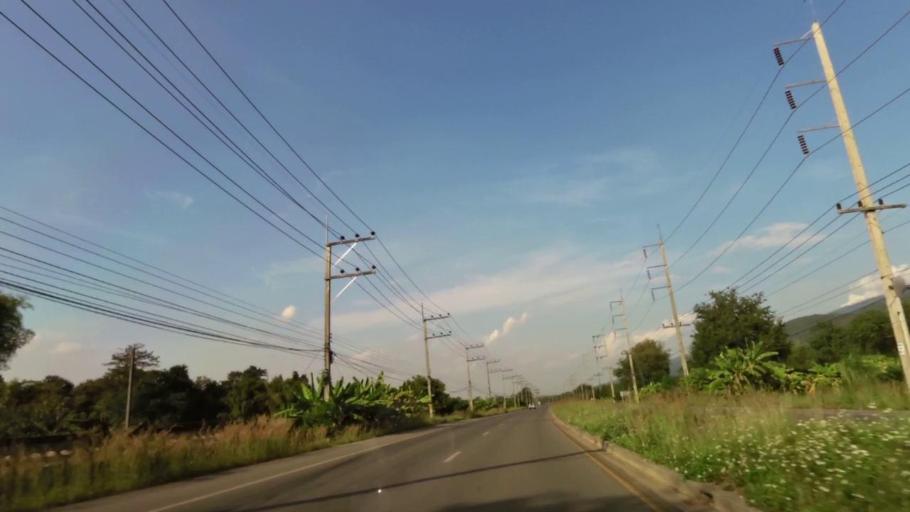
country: TH
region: Chiang Rai
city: Khun Tan
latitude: 19.8958
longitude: 100.2945
